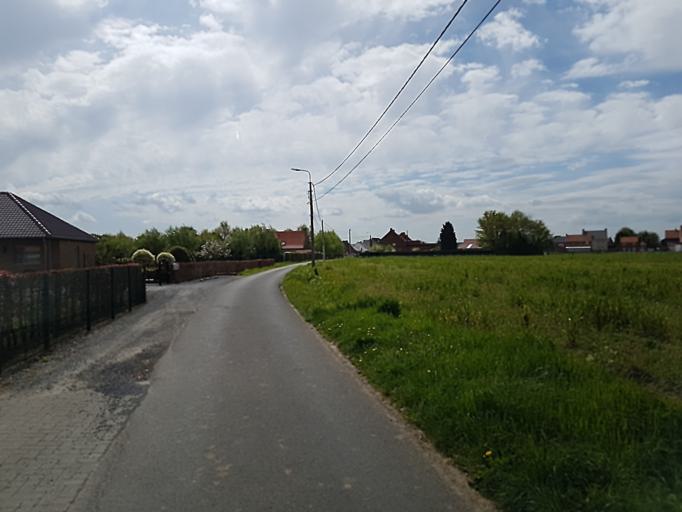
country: BE
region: Flanders
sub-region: Provincie West-Vlaanderen
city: Zonnebeke
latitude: 50.8399
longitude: 2.9839
